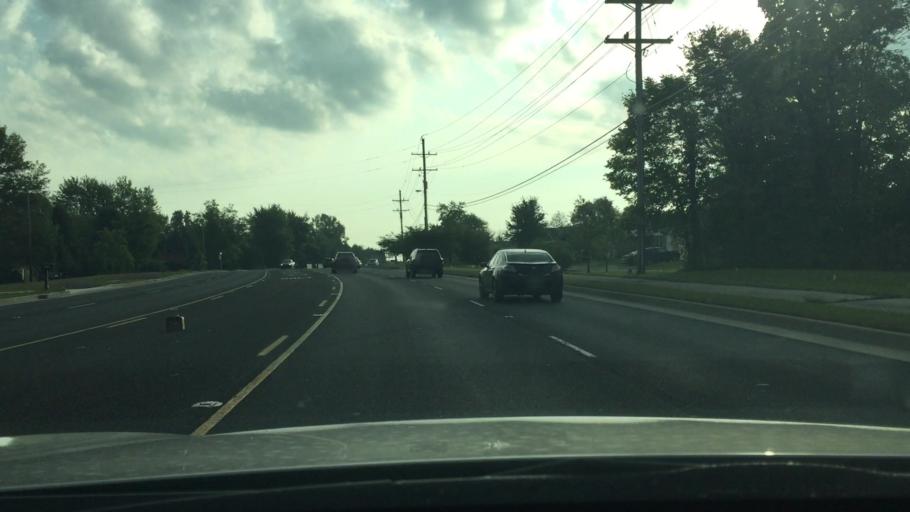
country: US
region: Indiana
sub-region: Hamilton County
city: Fishers
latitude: 40.0004
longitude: -86.0146
